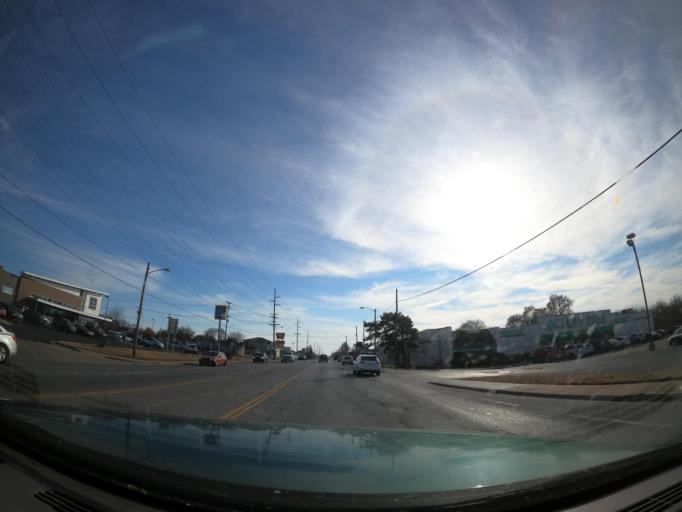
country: US
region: Oklahoma
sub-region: Tulsa County
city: Tulsa
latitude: 36.1242
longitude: -95.9403
